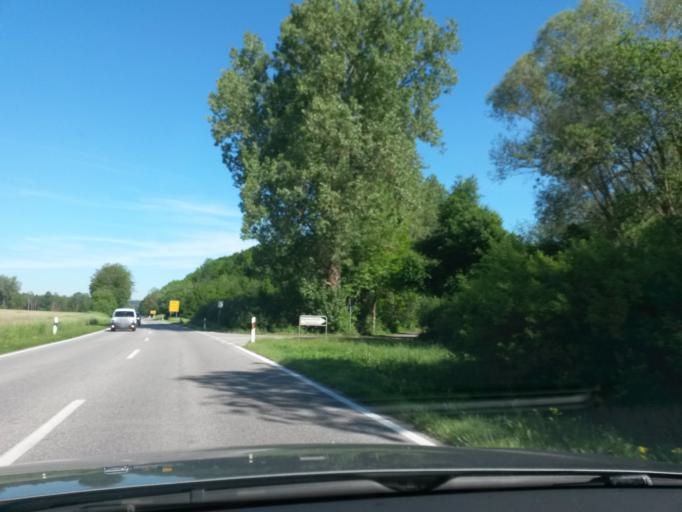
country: DE
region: Baden-Wuerttemberg
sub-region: Tuebingen Region
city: Durnau
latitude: 48.0650
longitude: 9.5782
